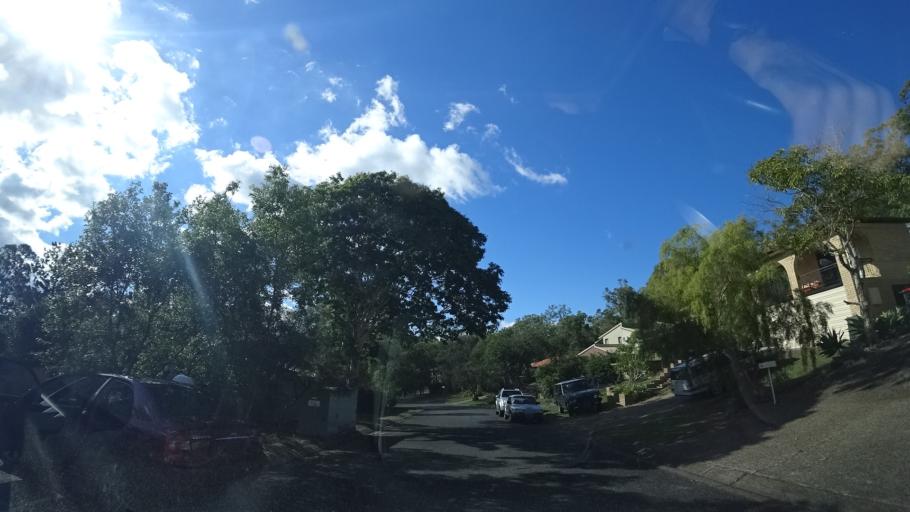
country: AU
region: Queensland
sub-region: Brisbane
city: Taringa
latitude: -27.4518
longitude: 152.9585
